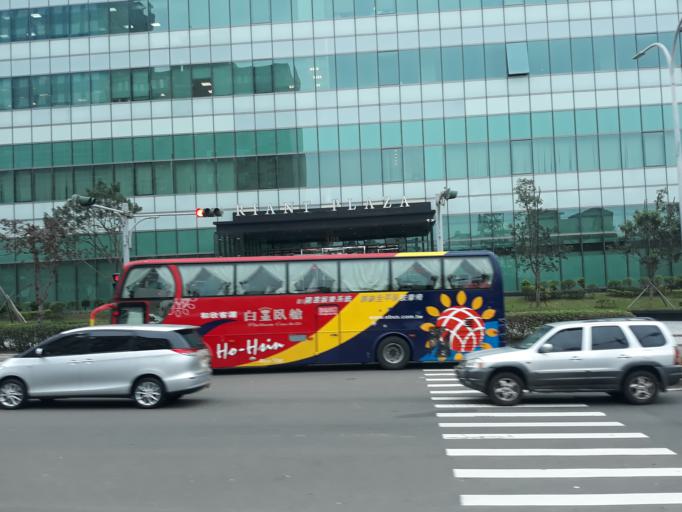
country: TW
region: Taiwan
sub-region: Hsinchu
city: Hsinchu
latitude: 24.7987
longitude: 121.0065
